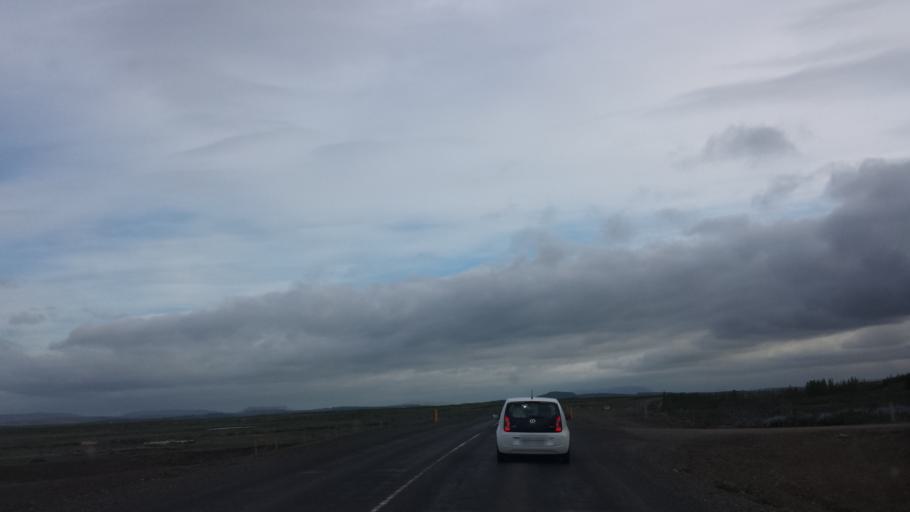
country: IS
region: South
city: Selfoss
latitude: 64.2861
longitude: -20.3403
